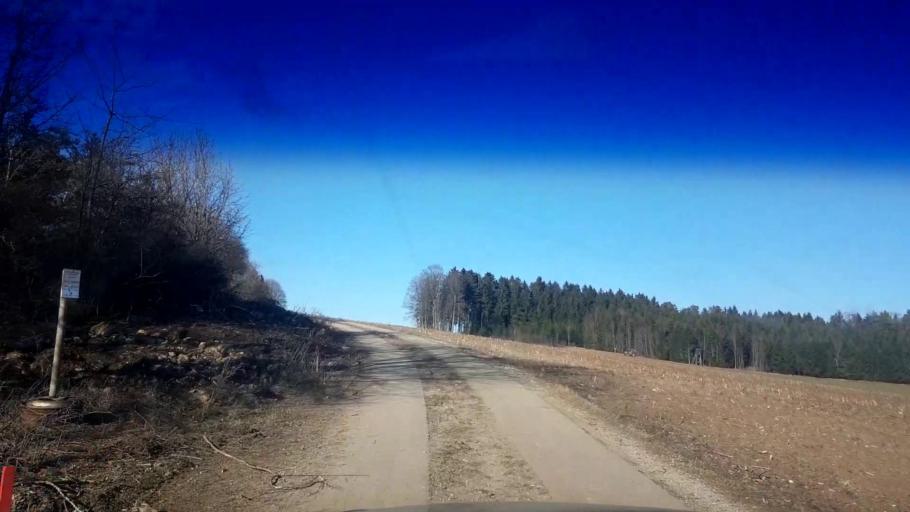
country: DE
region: Bavaria
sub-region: Upper Franconia
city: Poxdorf
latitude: 49.9600
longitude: 11.0866
